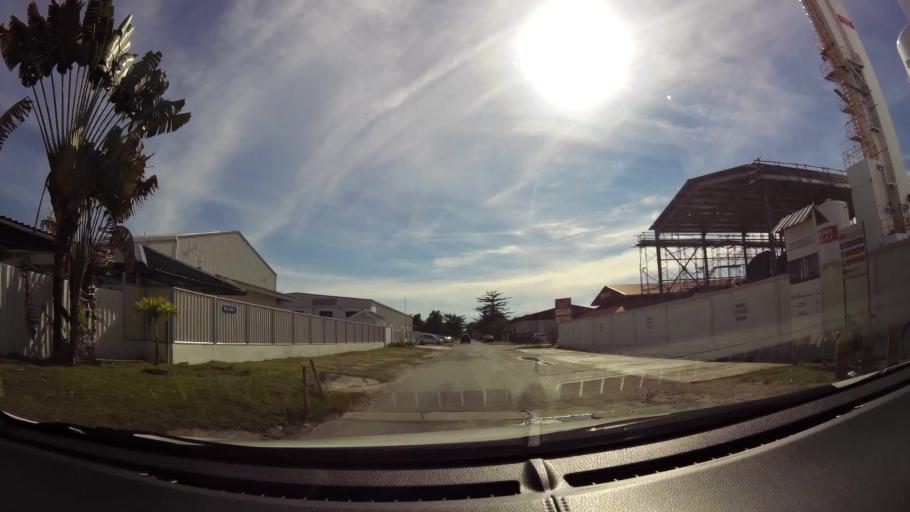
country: BN
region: Belait
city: Kuala Belait
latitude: 4.5716
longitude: 114.2076
